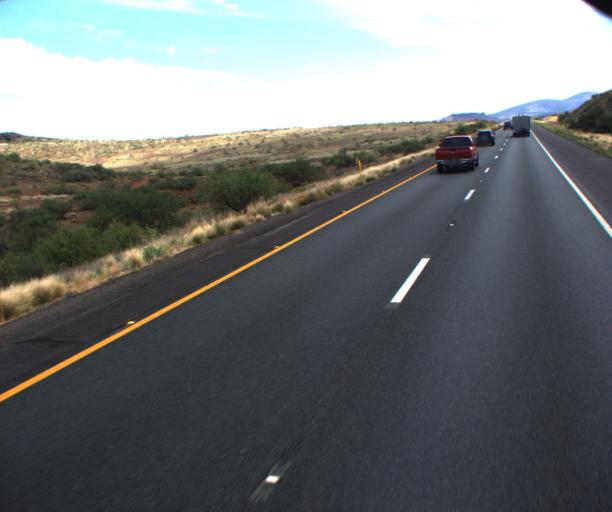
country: US
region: Arizona
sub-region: Yavapai County
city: Cordes Lakes
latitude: 34.4228
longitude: -112.0476
